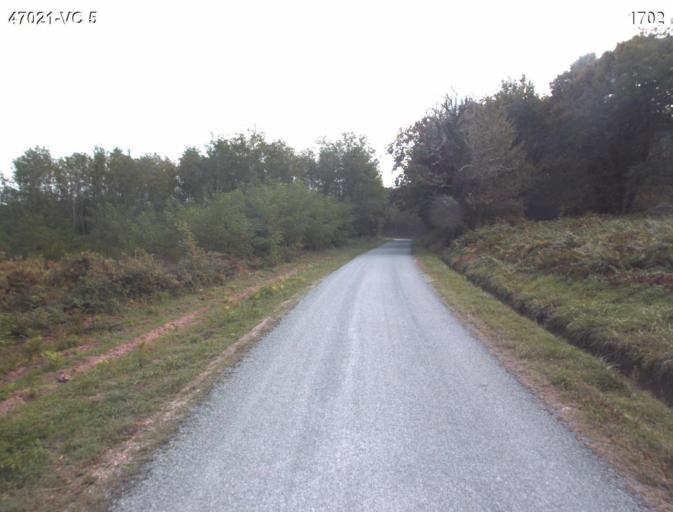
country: FR
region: Aquitaine
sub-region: Departement du Lot-et-Garonne
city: Barbaste
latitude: 44.1433
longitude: 0.2770
